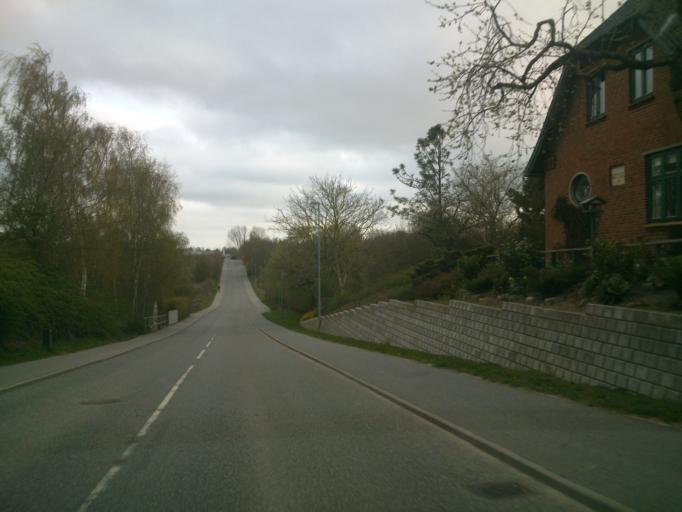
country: DK
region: South Denmark
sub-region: Fredericia Kommune
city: Fredericia
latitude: 55.5746
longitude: 9.7094
